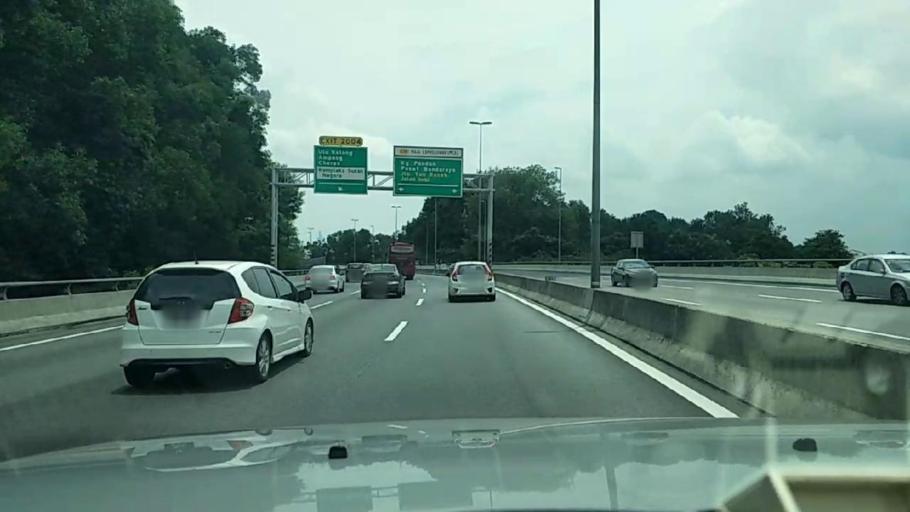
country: MY
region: Selangor
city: Kampong Baharu Balakong
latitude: 3.0582
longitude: 101.6884
